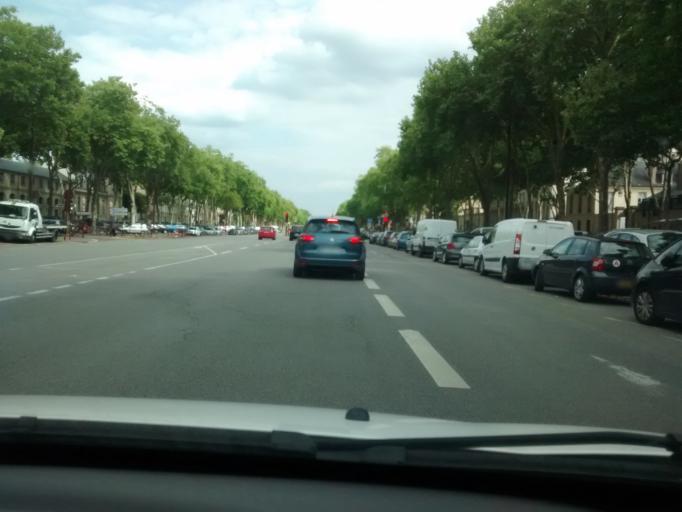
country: FR
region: Ile-de-France
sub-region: Departement des Yvelines
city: Versailles
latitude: 48.8014
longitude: 2.1328
